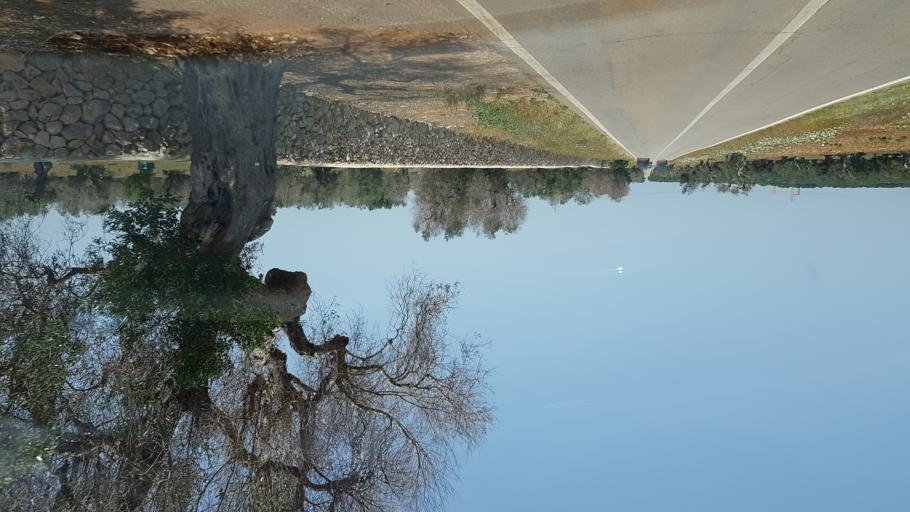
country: IT
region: Apulia
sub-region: Provincia di Lecce
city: Porto Cesareo
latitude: 40.2842
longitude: 17.9088
